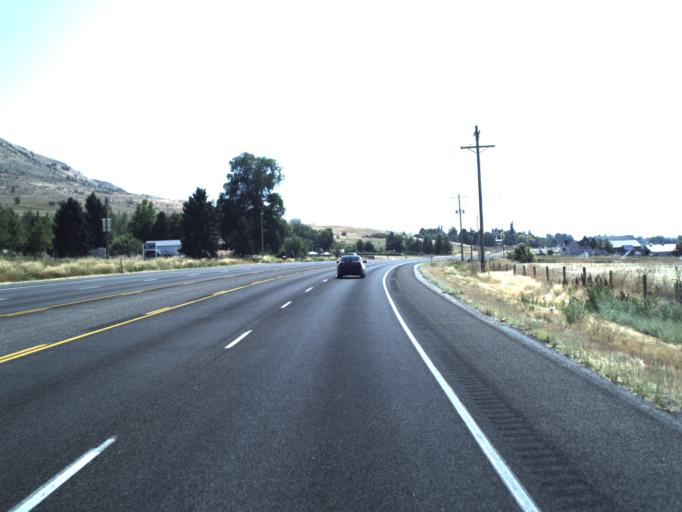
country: US
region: Utah
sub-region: Cache County
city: Richmond
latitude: 41.8912
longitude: -111.8152
